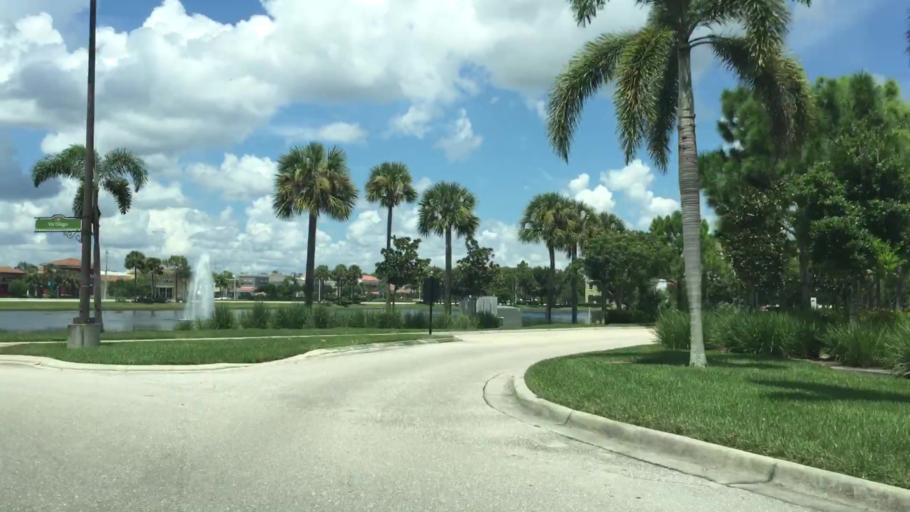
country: US
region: Florida
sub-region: Lee County
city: Estero
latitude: 26.4045
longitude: -81.8093
